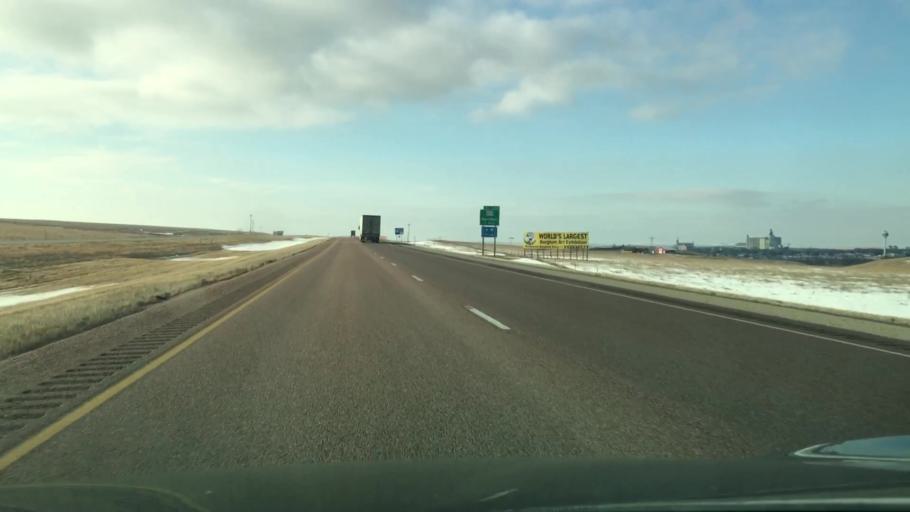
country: US
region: South Dakota
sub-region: Lyman County
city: Kennebec
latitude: 43.8885
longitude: -99.8418
